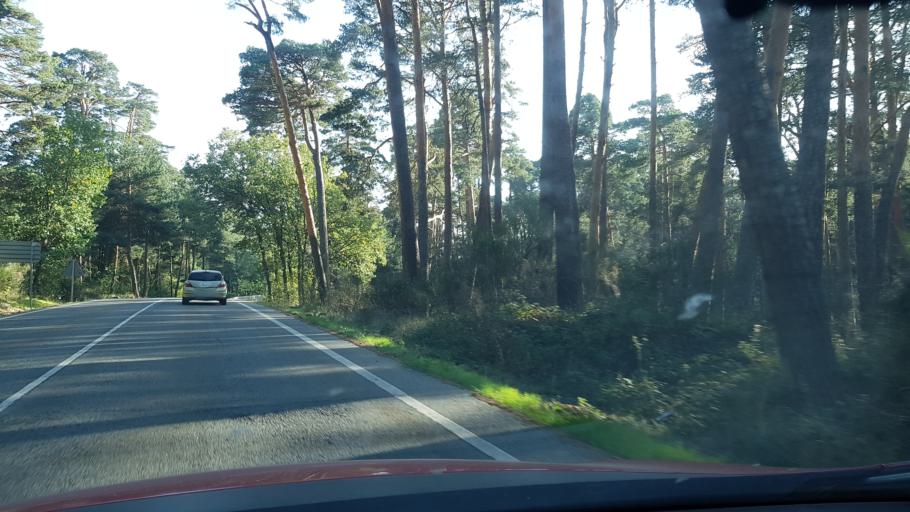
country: ES
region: Castille and Leon
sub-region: Provincia de Segovia
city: San Ildefonso
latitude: 40.8604
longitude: -4.0265
